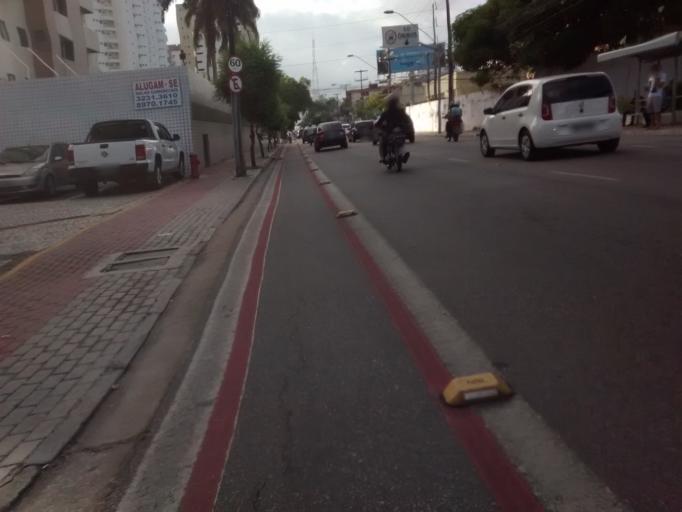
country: BR
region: Ceara
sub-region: Fortaleza
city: Fortaleza
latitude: -3.7440
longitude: -38.5070
